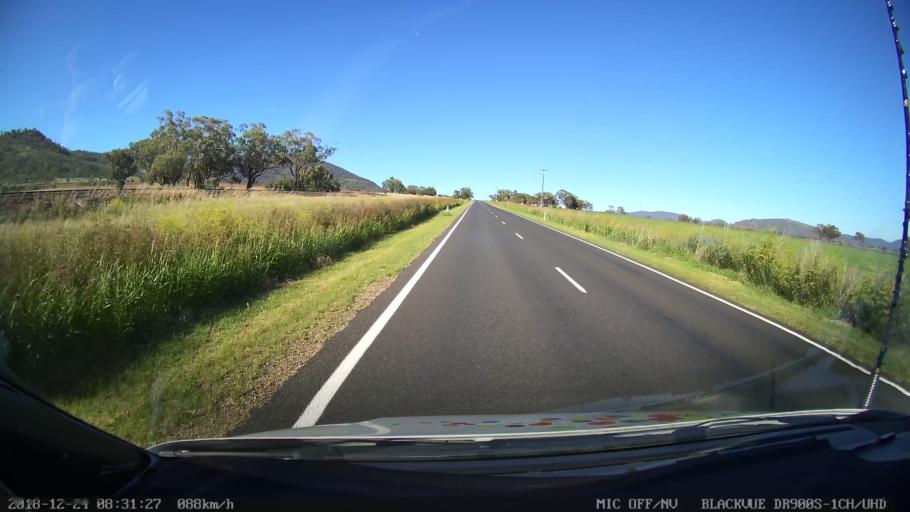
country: AU
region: New South Wales
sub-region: Tamworth Municipality
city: Phillip
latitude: -31.2736
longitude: 150.7113
